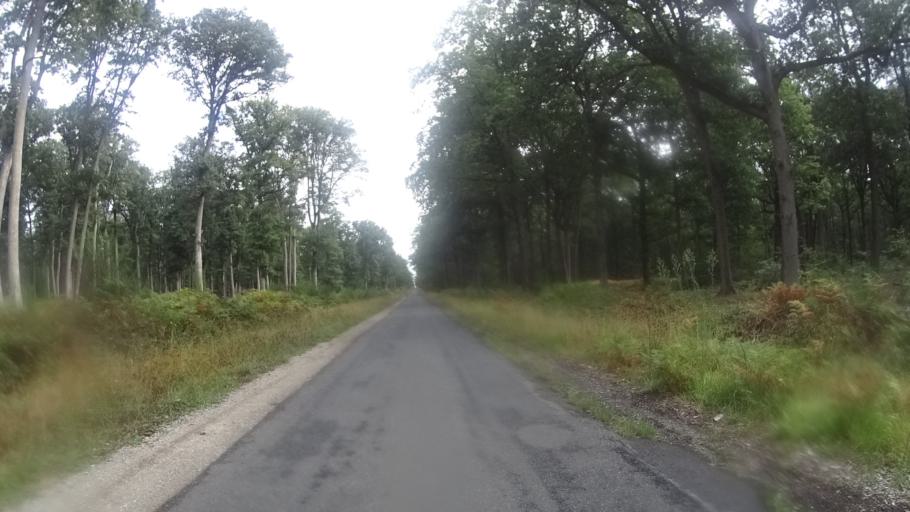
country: FR
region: Centre
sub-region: Departement du Loiret
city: Vitry-aux-Loges
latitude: 48.0172
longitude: 2.2519
